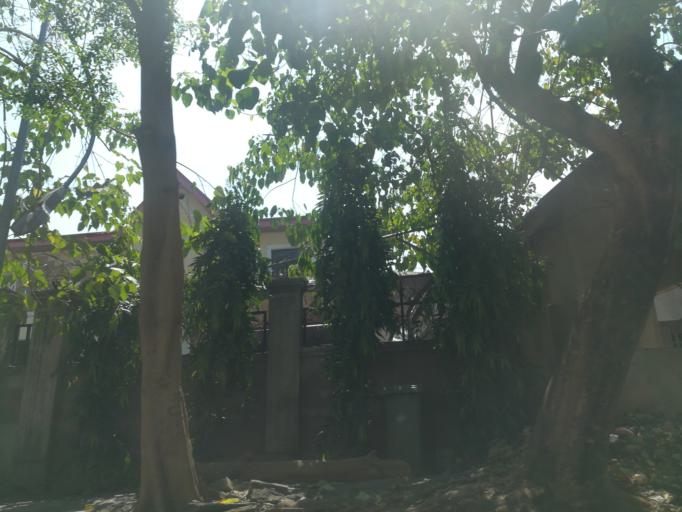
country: NG
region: Abuja Federal Capital Territory
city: Abuja
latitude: 9.0724
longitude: 7.4407
